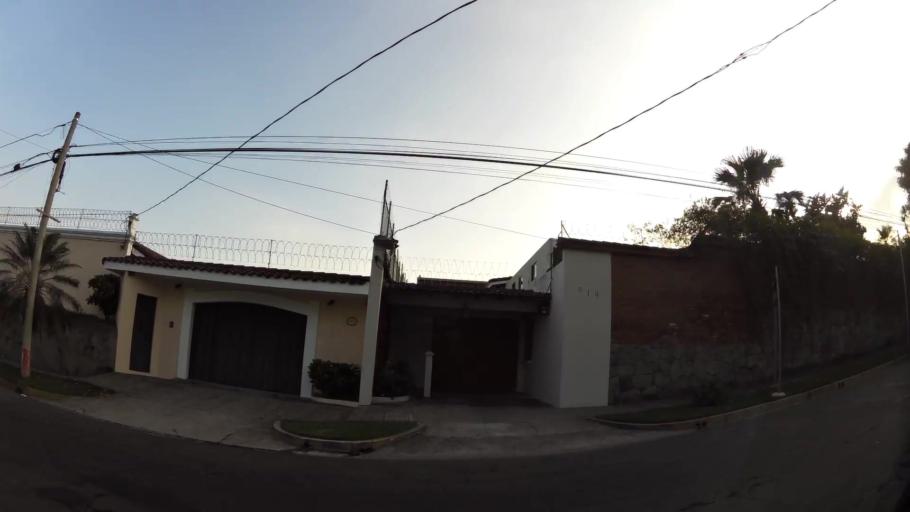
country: SV
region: La Libertad
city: Antiguo Cuscatlan
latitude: 13.6971
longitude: -89.2460
